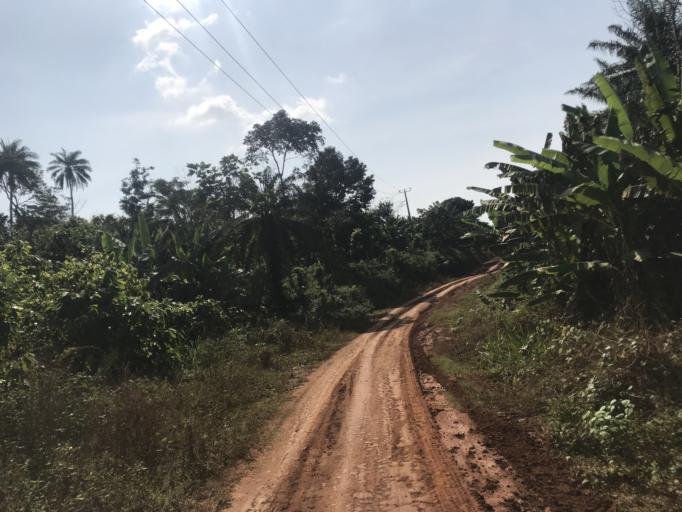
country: NG
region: Osun
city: Osu
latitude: 7.6341
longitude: 4.6692
